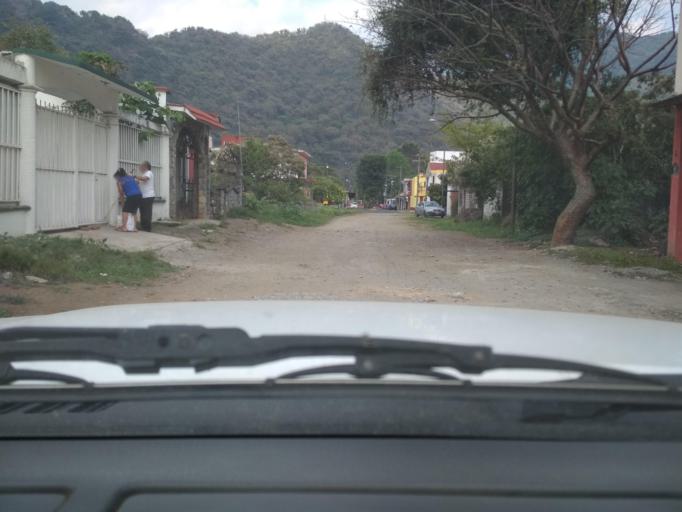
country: MX
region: Veracruz
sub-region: Mariano Escobedo
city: Palmira
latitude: 18.8719
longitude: -97.1008
